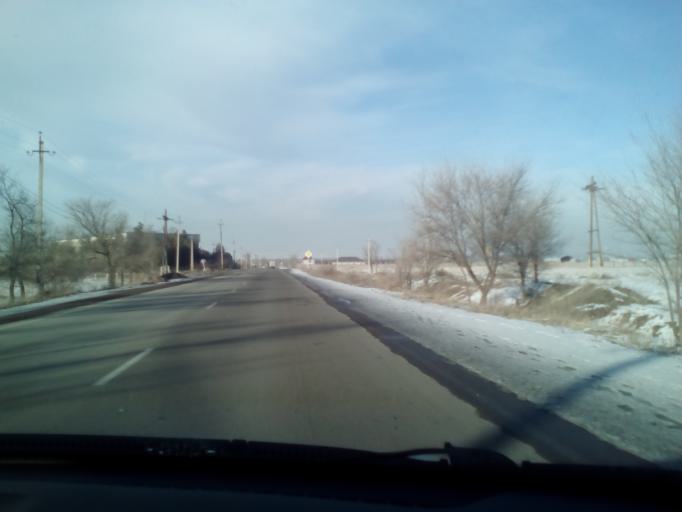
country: KZ
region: Almaty Oblysy
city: Burunday
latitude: 43.1979
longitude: 76.4148
